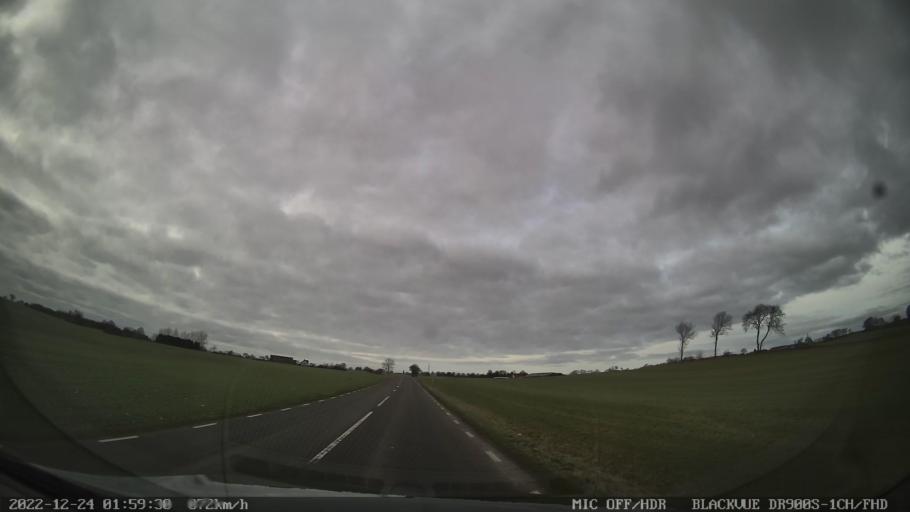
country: SE
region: Skane
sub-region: Tomelilla Kommun
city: Tomelilla
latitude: 55.6084
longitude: 14.0145
